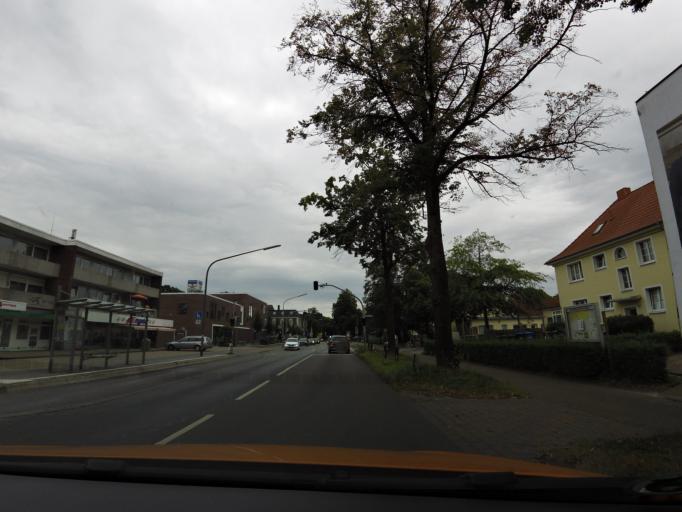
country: DE
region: Lower Saxony
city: Oldenburg
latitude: 53.1695
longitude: 8.1970
